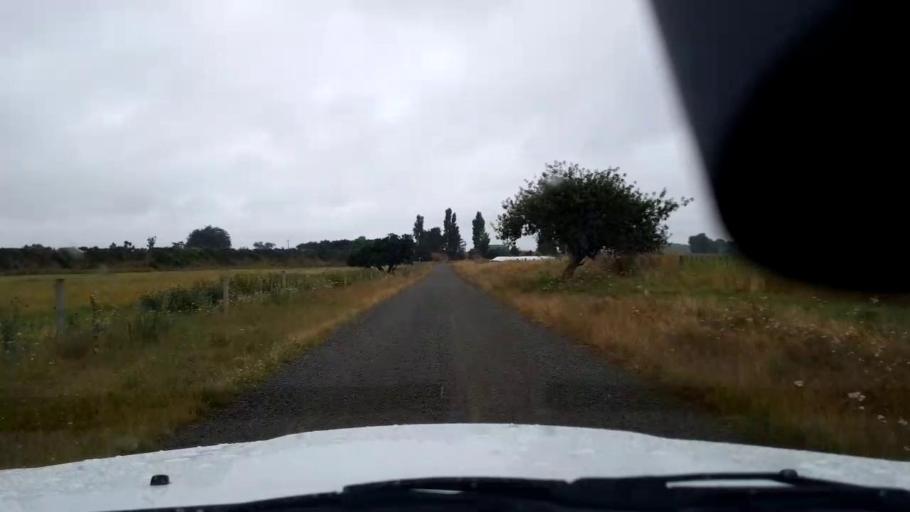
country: NZ
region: Canterbury
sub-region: Timaru District
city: Pleasant Point
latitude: -44.2533
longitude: 171.2151
